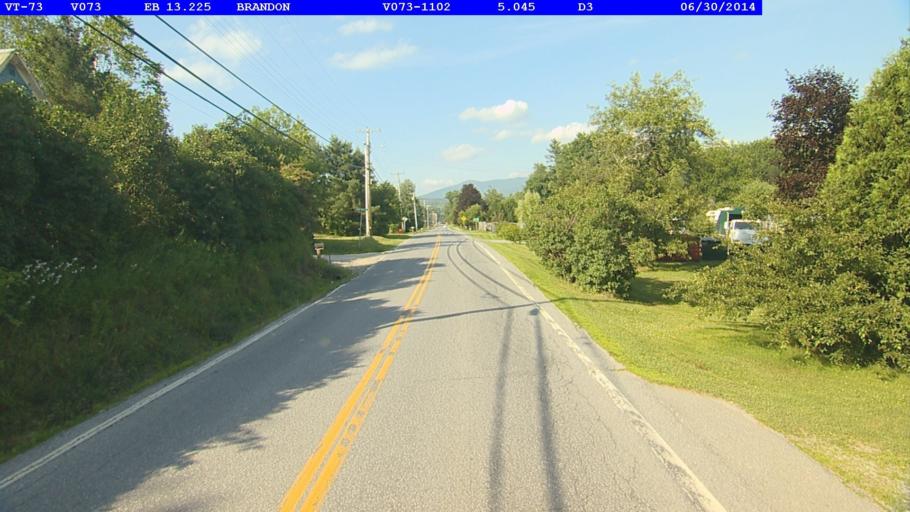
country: US
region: Vermont
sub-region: Rutland County
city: Brandon
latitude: 43.8175
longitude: -73.0634
